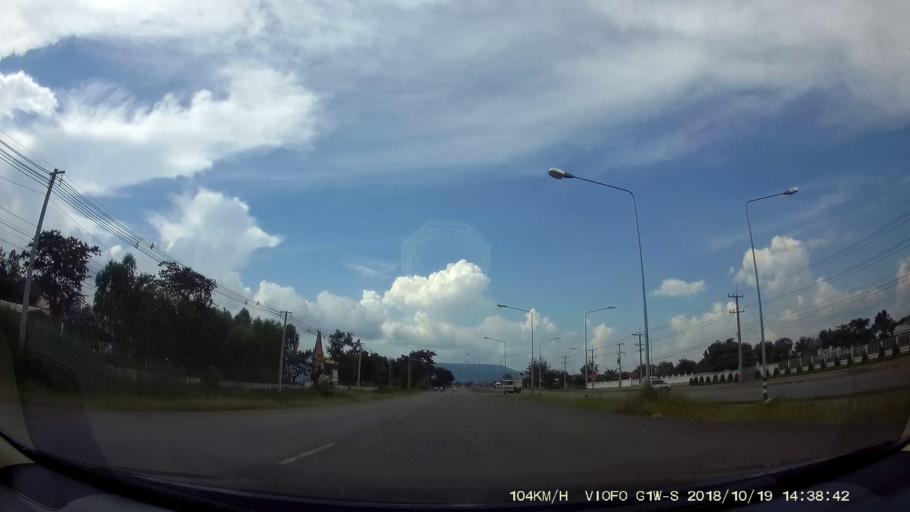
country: TH
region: Chaiyaphum
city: Kaeng Khro
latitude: 16.2167
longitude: 102.1999
